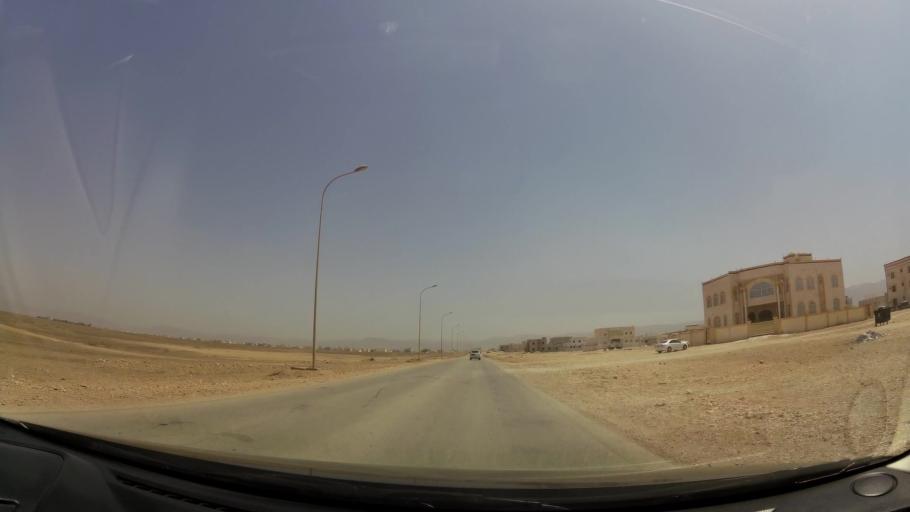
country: OM
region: Zufar
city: Salalah
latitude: 17.0585
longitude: 54.2109
